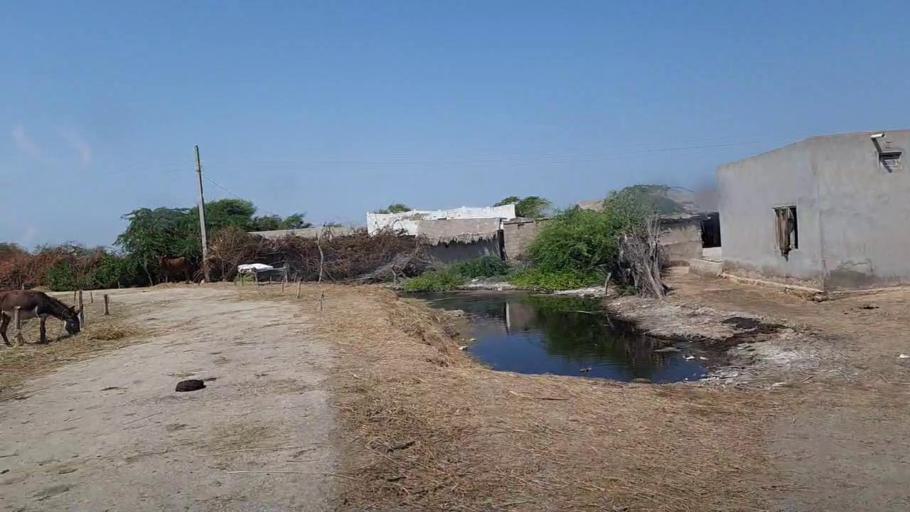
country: PK
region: Sindh
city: Mirpur Batoro
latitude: 24.6454
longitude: 68.4521
